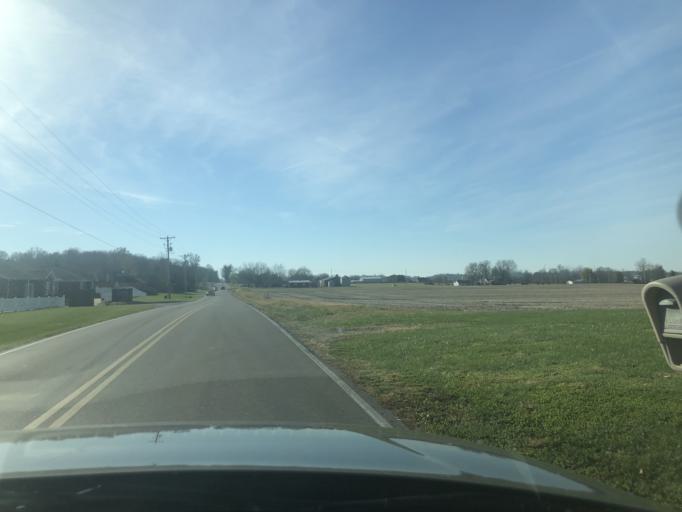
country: US
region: Indiana
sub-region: Warrick County
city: Newburgh
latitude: 37.9950
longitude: -87.4138
